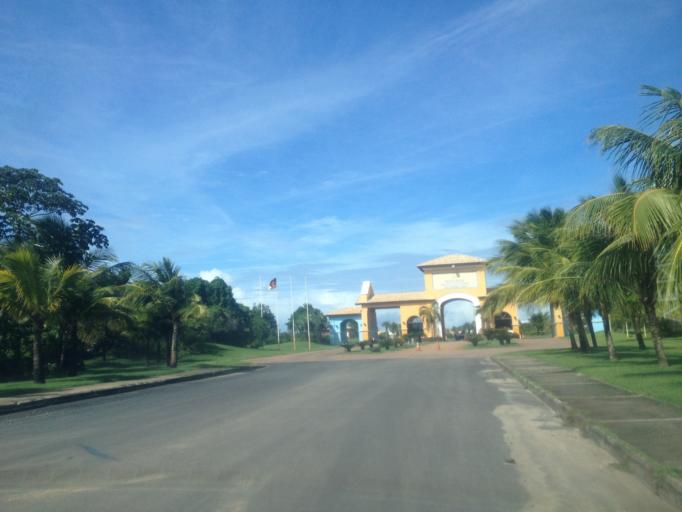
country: BR
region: Bahia
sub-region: Mata De Sao Joao
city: Mata de Sao Joao
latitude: -12.5424
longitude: -37.9918
